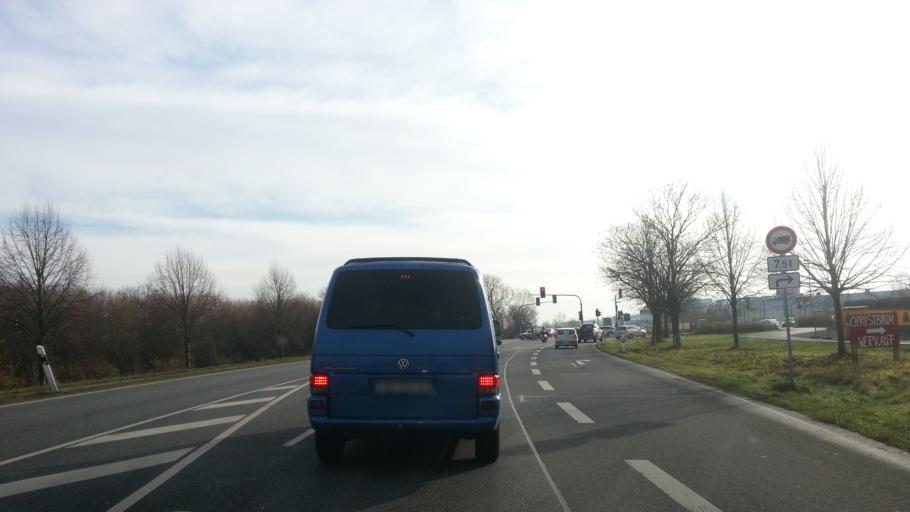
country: DE
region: Hesse
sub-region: Regierungsbezirk Darmstadt
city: Gross-Gerau
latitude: 49.9136
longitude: 8.4965
